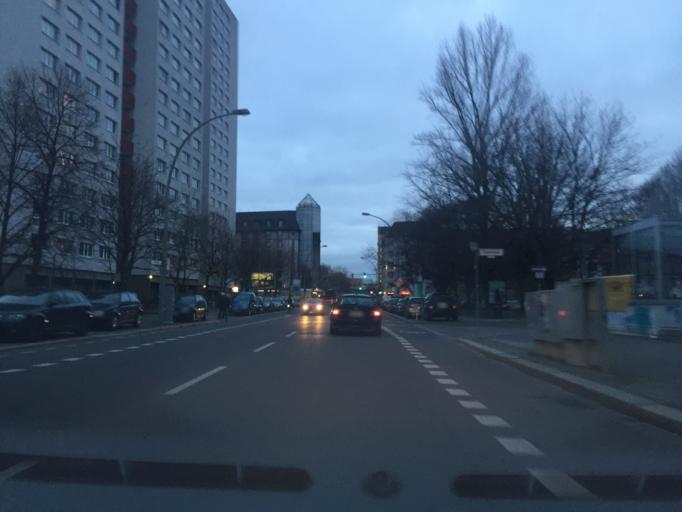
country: DE
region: Berlin
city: Mitte
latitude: 52.5134
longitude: 13.4067
